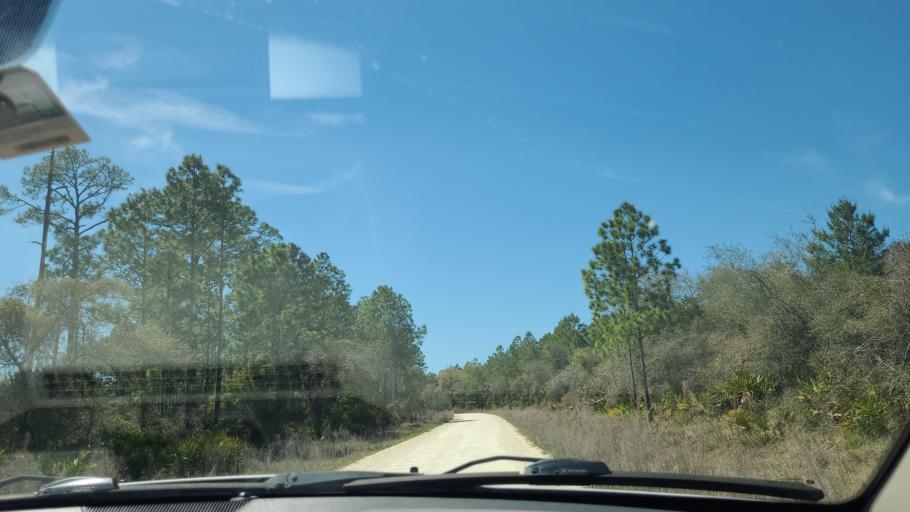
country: US
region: Florida
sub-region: Putnam County
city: Interlachen
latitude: 29.4394
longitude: -81.7701
